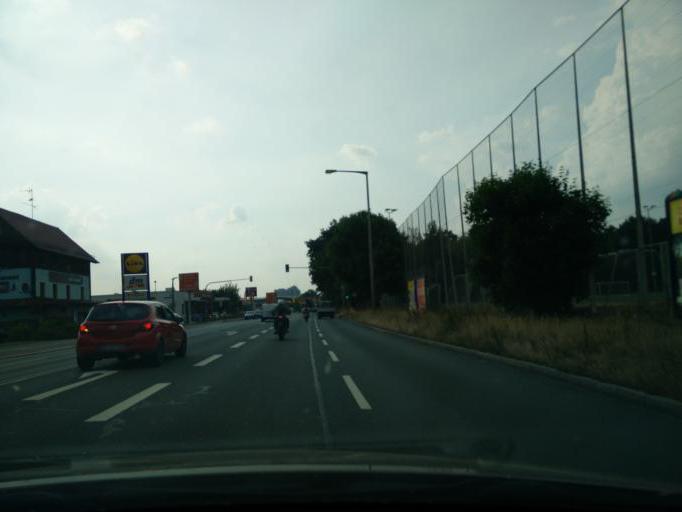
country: DE
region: Bavaria
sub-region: Regierungsbezirk Mittelfranken
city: Nuernberg
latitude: 49.4340
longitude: 11.1273
